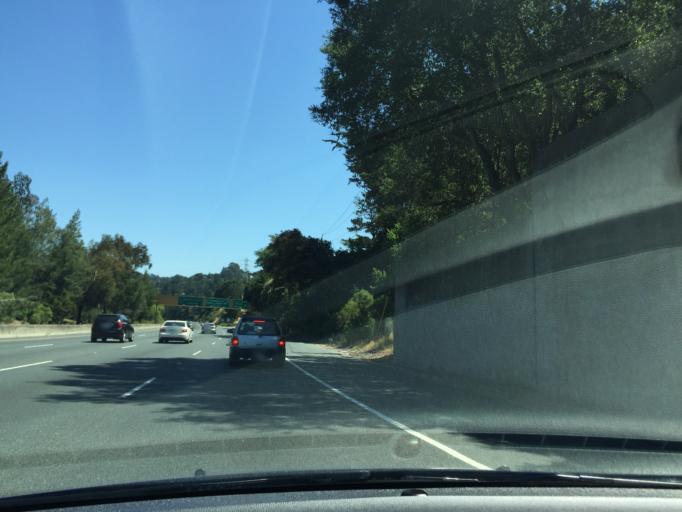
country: US
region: California
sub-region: Contra Costa County
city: Orinda
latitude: 37.8741
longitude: -122.1874
